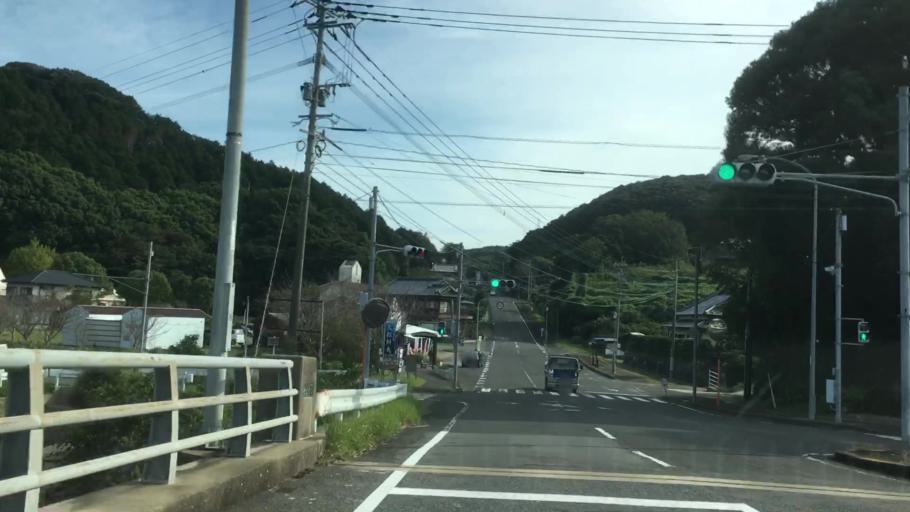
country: JP
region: Nagasaki
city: Sasebo
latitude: 32.9945
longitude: 129.6531
